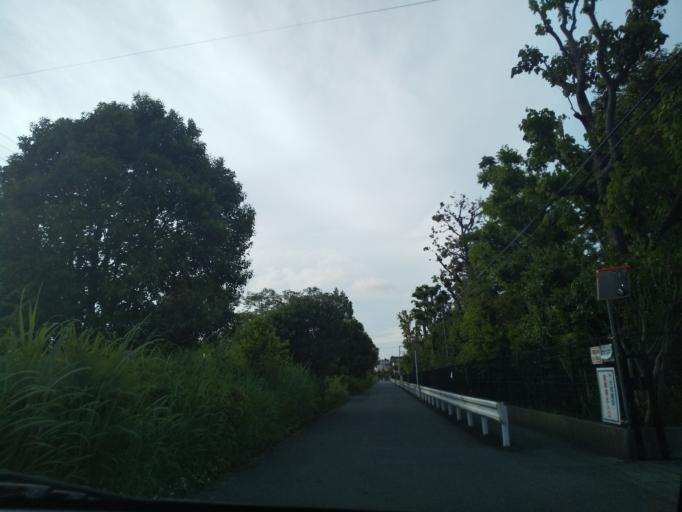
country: JP
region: Kanagawa
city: Zama
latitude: 35.5394
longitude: 139.3914
